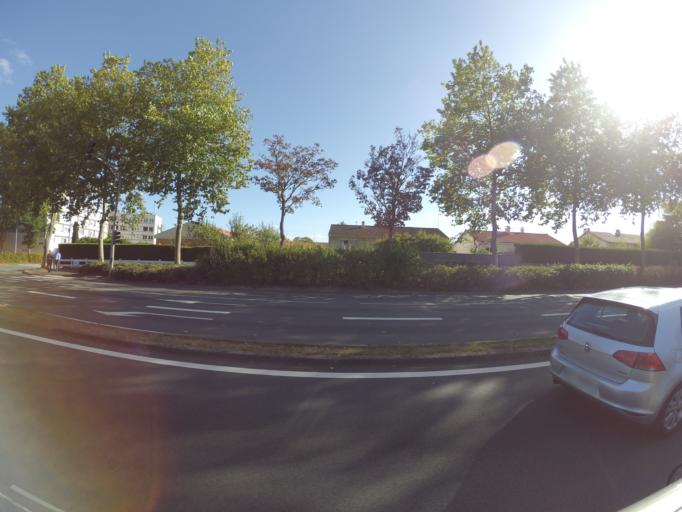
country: FR
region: Pays de la Loire
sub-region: Departement de Maine-et-Loire
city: Cholet
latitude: 47.0444
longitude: -0.8818
